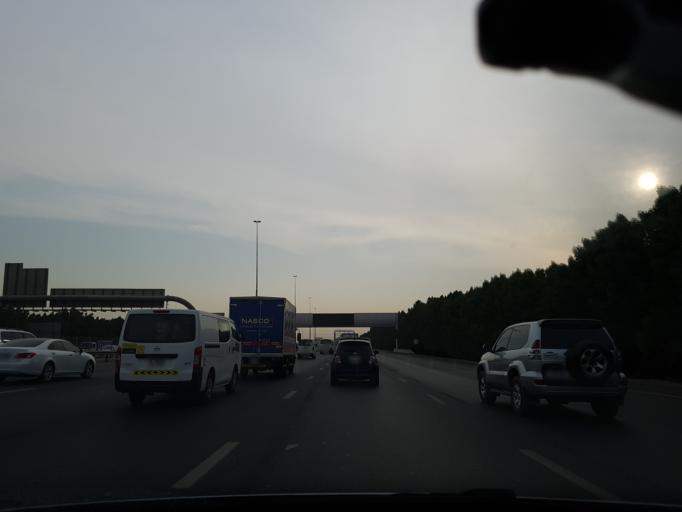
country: AE
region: Ash Shariqah
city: Sharjah
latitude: 25.2695
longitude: 55.4146
